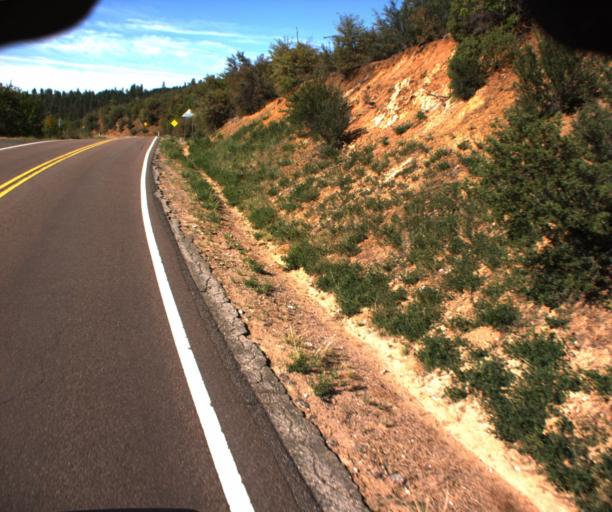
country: US
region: Arizona
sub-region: Yavapai County
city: Prescott
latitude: 34.4902
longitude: -112.5007
